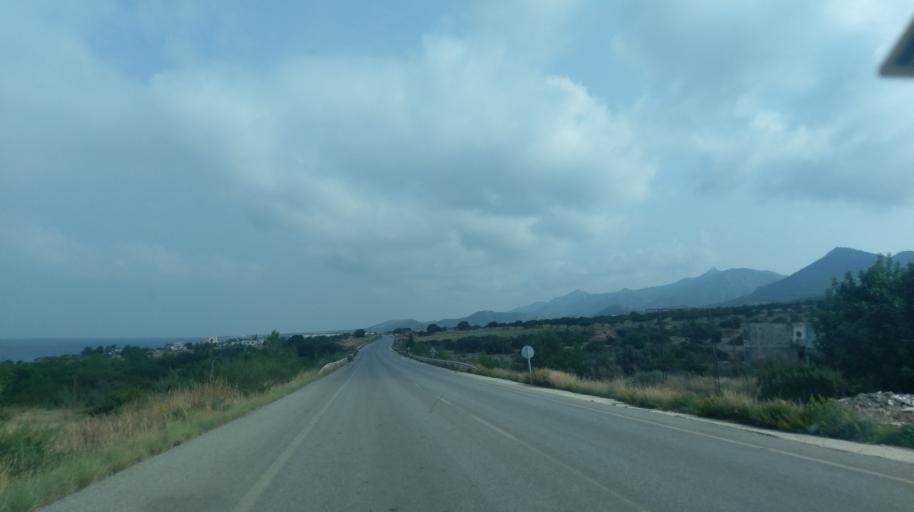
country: CY
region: Ammochostos
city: Lefkonoiko
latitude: 35.3583
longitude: 33.6596
